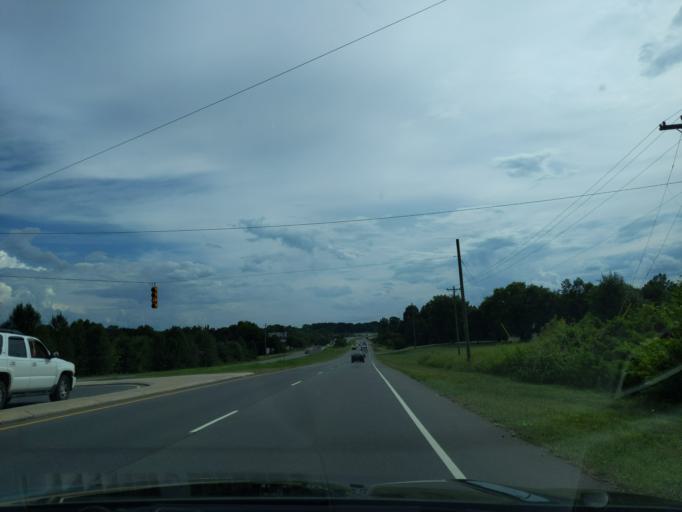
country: US
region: North Carolina
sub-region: Cabarrus County
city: Harrisburg
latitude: 35.3447
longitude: -80.6103
